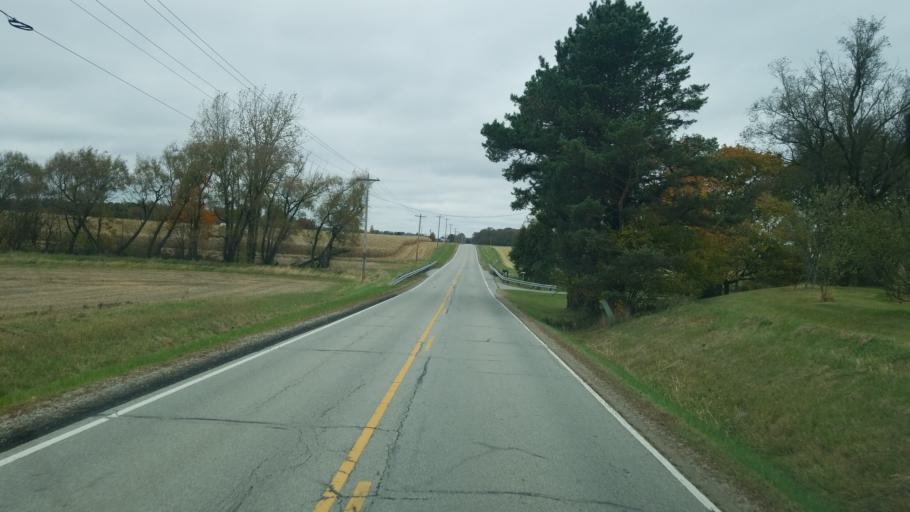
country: US
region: Ohio
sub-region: Huron County
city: Willard
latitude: 40.9850
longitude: -82.8533
